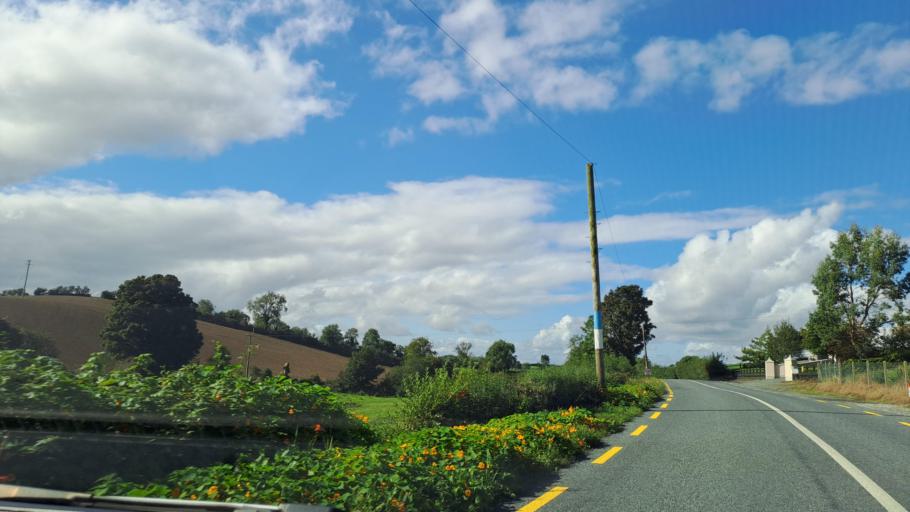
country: IE
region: Ulster
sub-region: An Cabhan
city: Kingscourt
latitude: 53.9742
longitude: -6.8723
